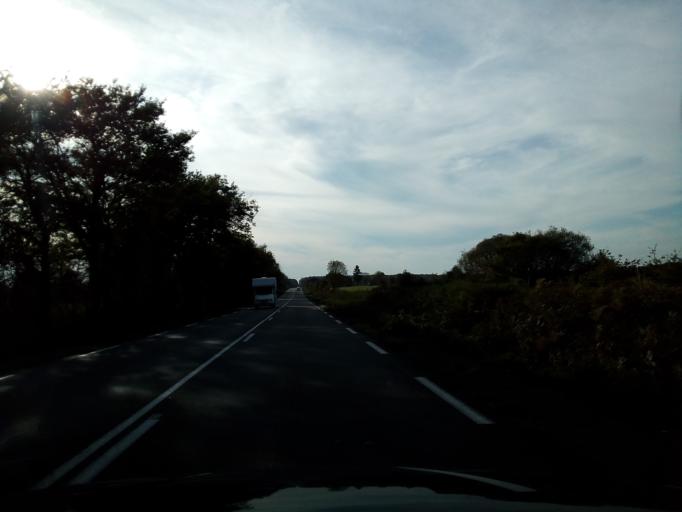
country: FR
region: Limousin
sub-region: Departement de la Haute-Vienne
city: Peyrat-de-Bellac
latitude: 46.1212
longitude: 0.9611
